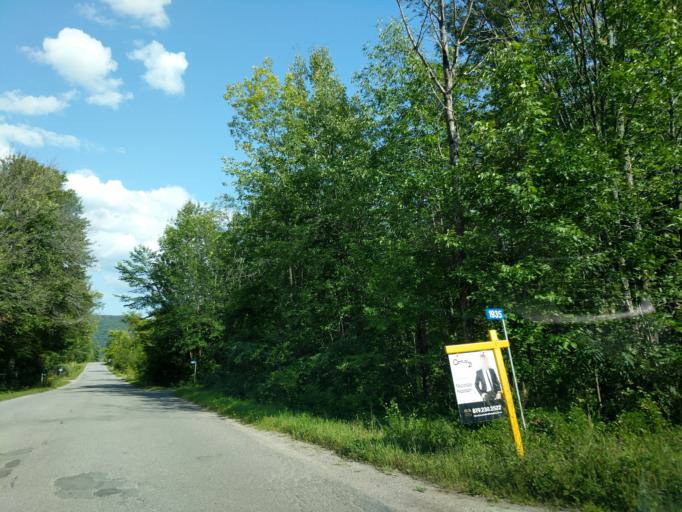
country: CA
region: Quebec
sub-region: Outaouais
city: Wakefield
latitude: 45.5032
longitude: -75.9496
